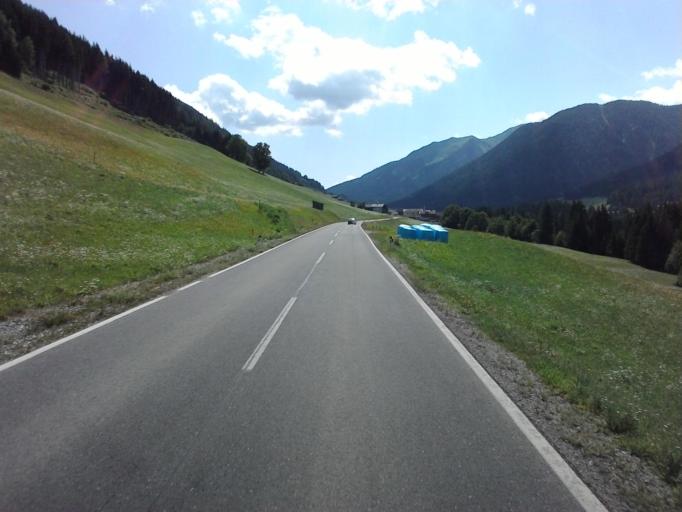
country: AT
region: Tyrol
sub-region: Politischer Bezirk Lienz
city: Strassen
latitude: 46.7352
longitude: 12.4792
